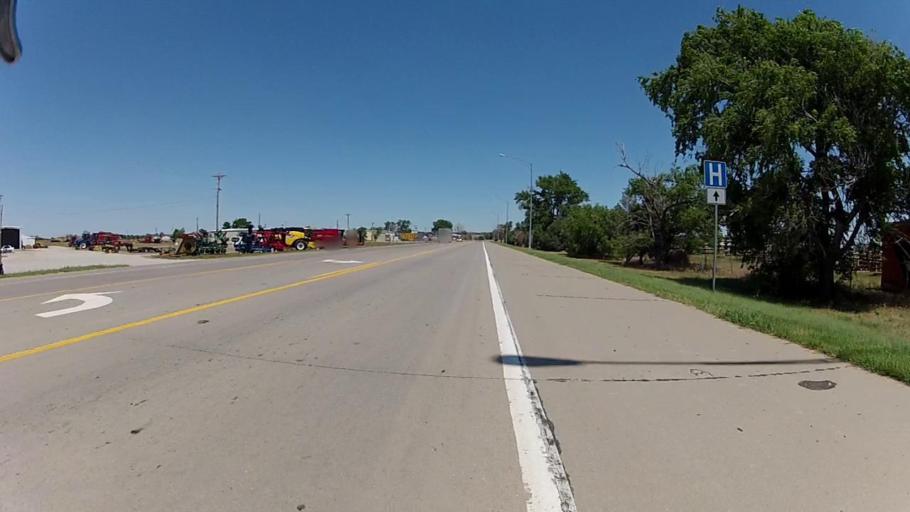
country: US
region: Kansas
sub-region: Ford County
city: Dodge City
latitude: 37.7264
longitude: -100.0168
